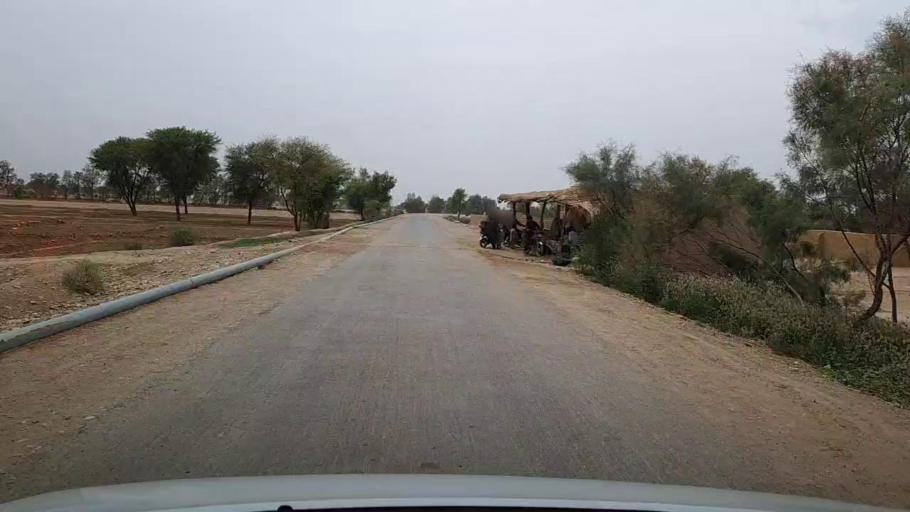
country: PK
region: Sindh
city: Sehwan
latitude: 26.3220
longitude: 67.7297
